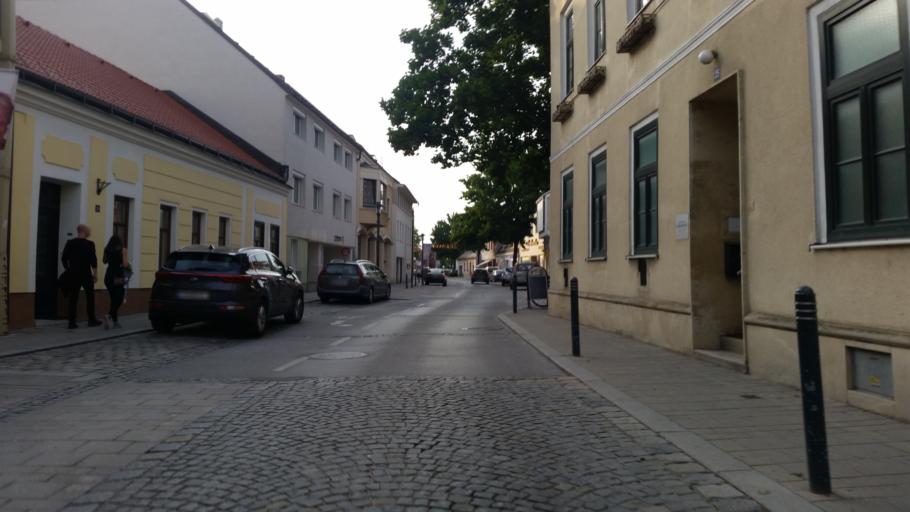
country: AT
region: Lower Austria
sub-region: Politischer Bezirk Mistelbach
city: Wolkersdorf im Weinviertel
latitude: 48.3837
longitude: 16.5173
